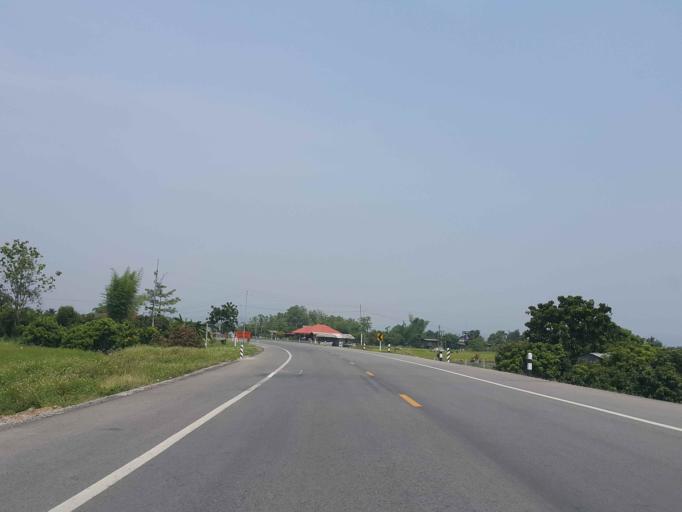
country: TH
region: Chiang Mai
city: Mae Taeng
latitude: 19.0692
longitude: 98.9561
